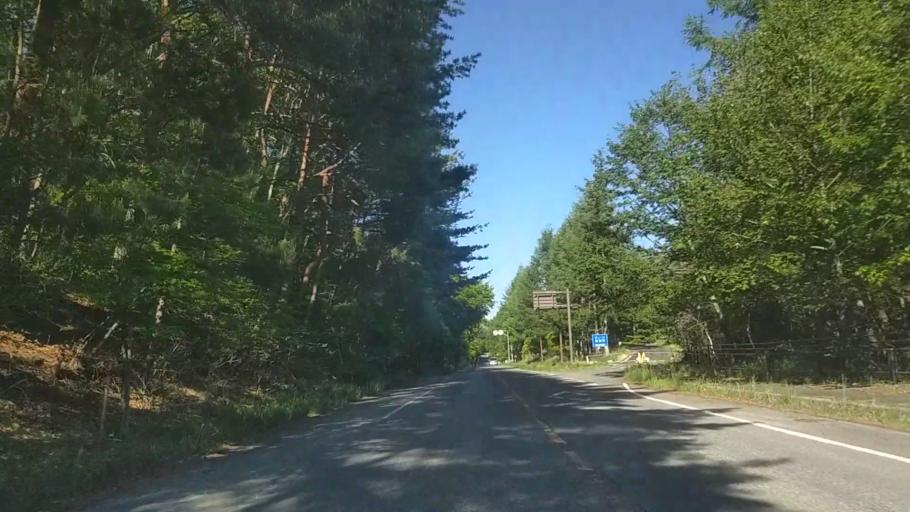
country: JP
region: Nagano
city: Chino
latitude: 35.8983
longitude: 138.3301
